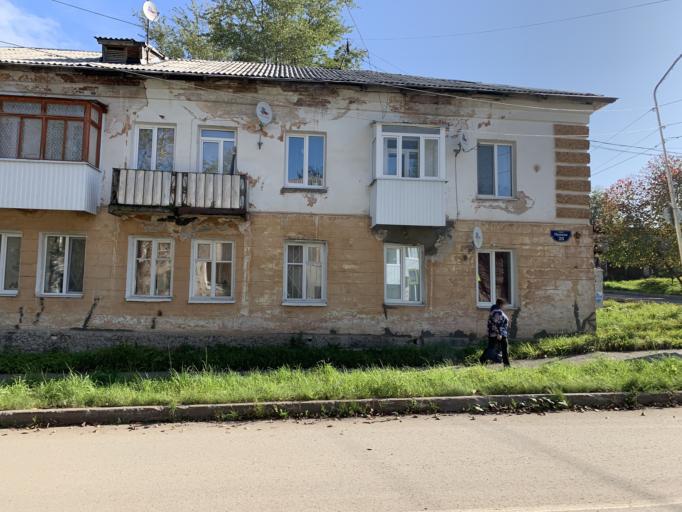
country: RU
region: Perm
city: Gubakha
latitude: 58.8407
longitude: 57.5549
